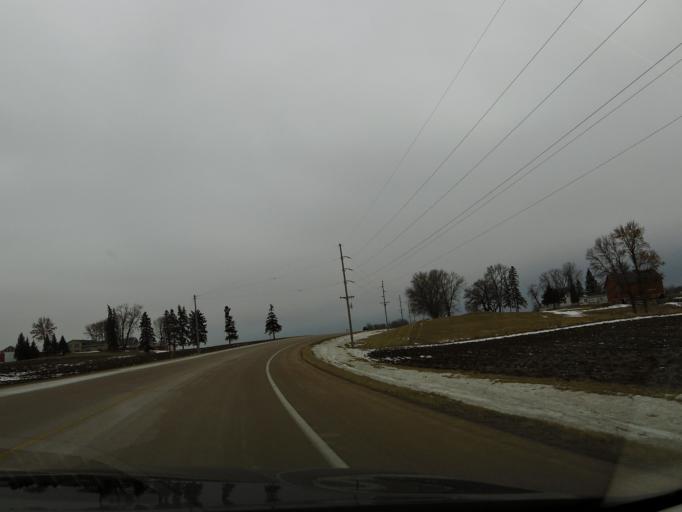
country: US
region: Minnesota
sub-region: Carver County
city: Watertown
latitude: 44.9465
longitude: -93.8340
